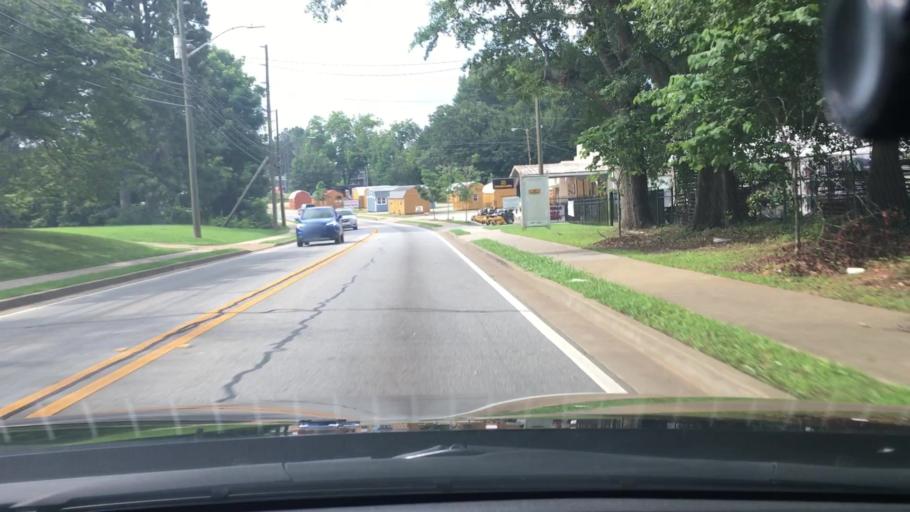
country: US
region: Georgia
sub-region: Coweta County
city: East Newnan
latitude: 33.3582
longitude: -84.7910
